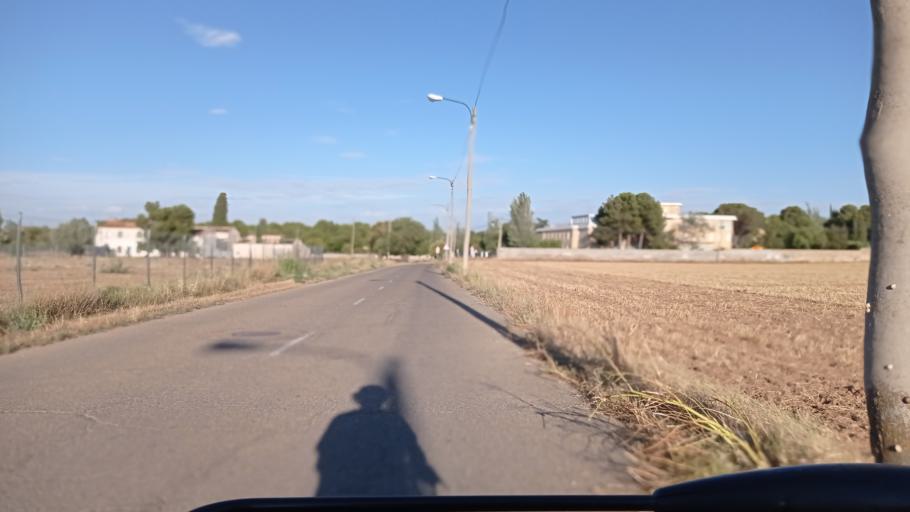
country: ES
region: Aragon
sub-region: Provincia de Zaragoza
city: Oliver-Valdefierro, Oliver, Valdefierro
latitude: 41.6757
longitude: -0.9627
